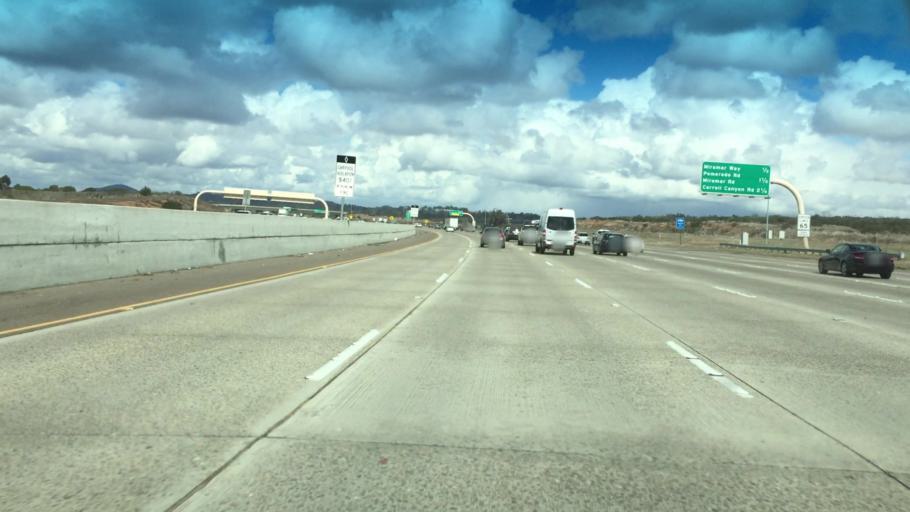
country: US
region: California
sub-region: San Diego County
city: Poway
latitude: 32.8674
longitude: -117.1082
